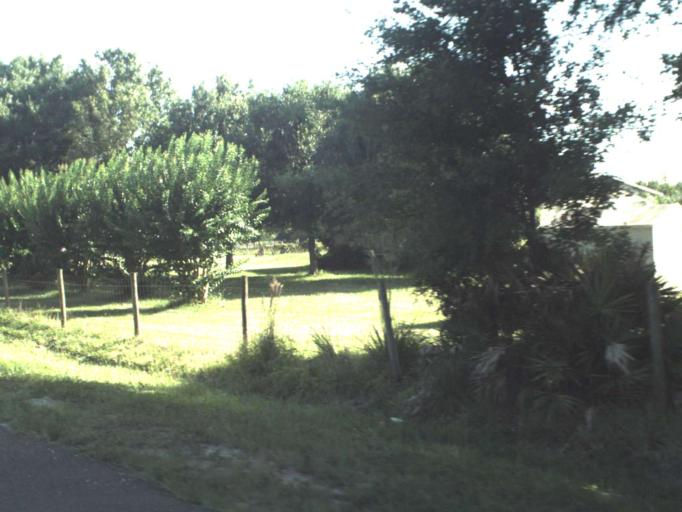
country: US
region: Florida
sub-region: Lake County
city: Groveland
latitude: 28.4138
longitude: -81.8310
